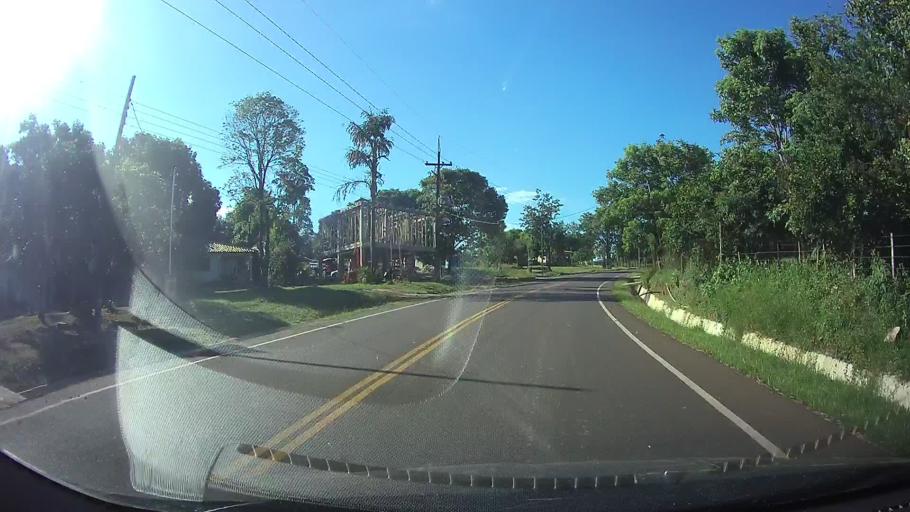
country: PY
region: Cordillera
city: Caacupe
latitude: -25.3475
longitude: -57.1521
